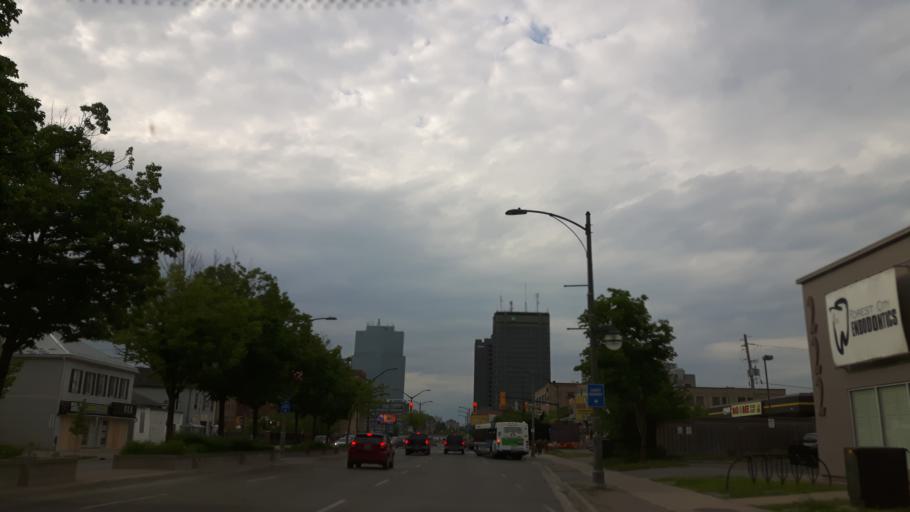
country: CA
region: Ontario
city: London
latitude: 42.9793
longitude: -81.2423
